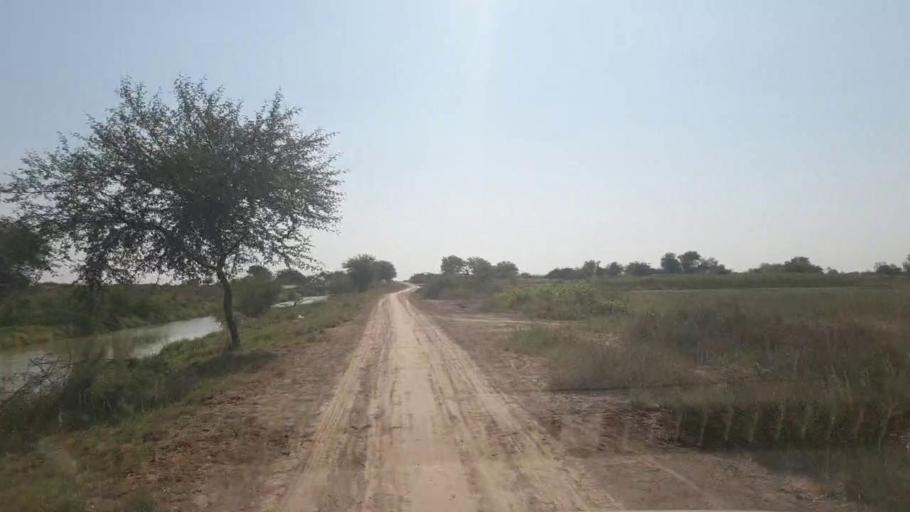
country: PK
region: Sindh
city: Tando Bago
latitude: 24.8887
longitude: 69.1645
